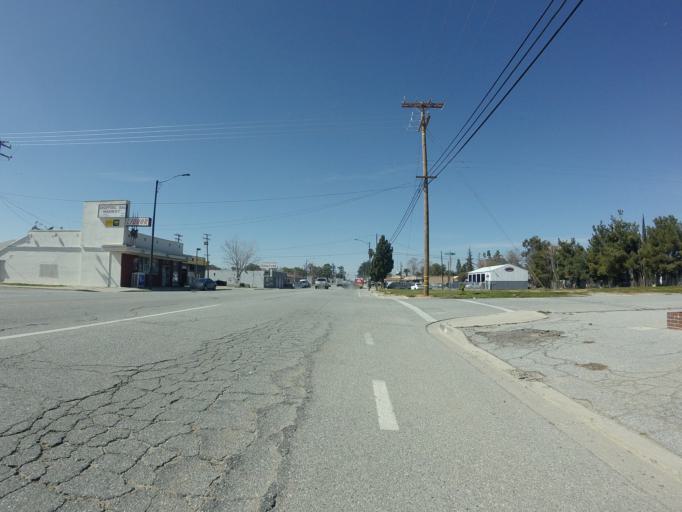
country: US
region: California
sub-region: Riverside County
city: Beaumont
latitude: 33.9295
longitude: -116.9687
